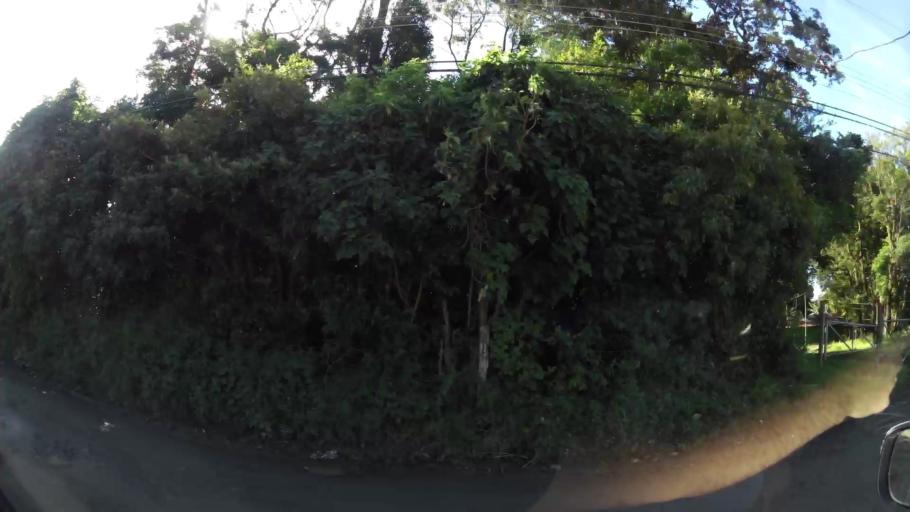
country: CR
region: Guanacaste
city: Juntas
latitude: 10.3138
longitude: -84.8180
